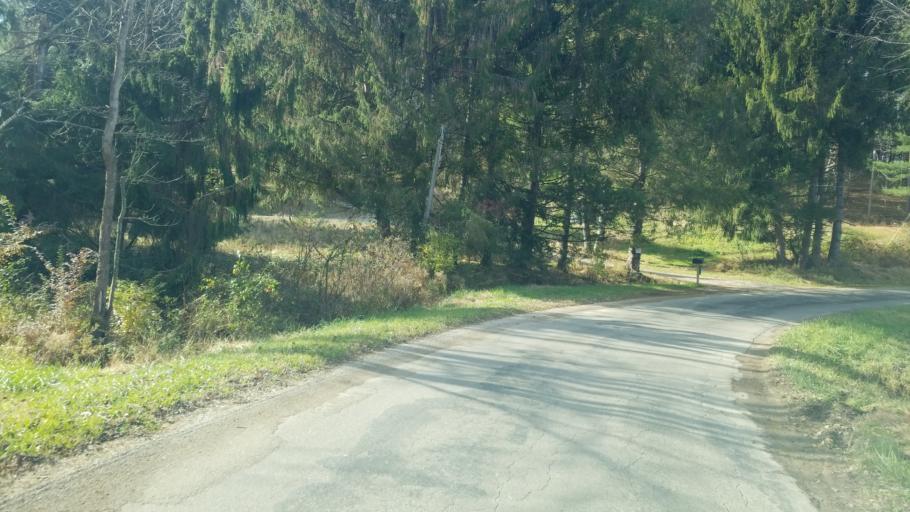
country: US
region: Ohio
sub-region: Licking County
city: Newark
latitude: 40.1397
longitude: -82.3547
